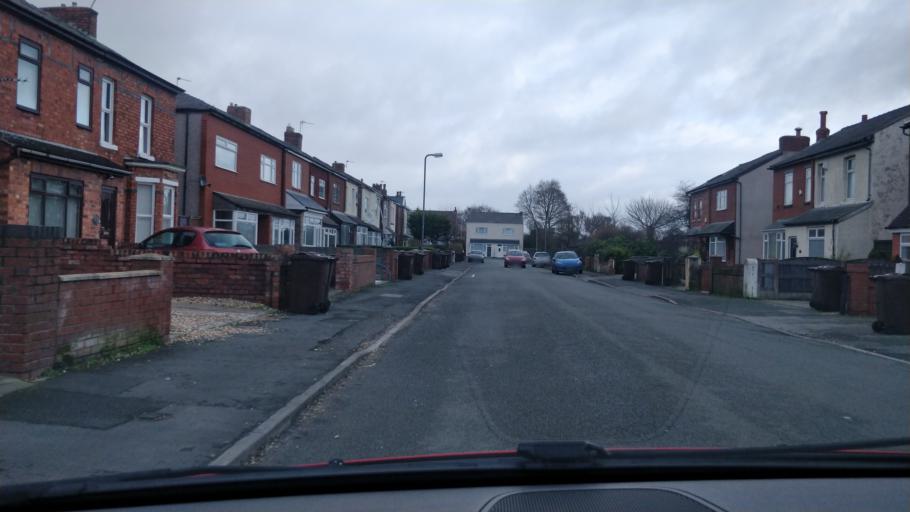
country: GB
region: England
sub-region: Sefton
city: Southport
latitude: 53.6307
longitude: -3.0038
